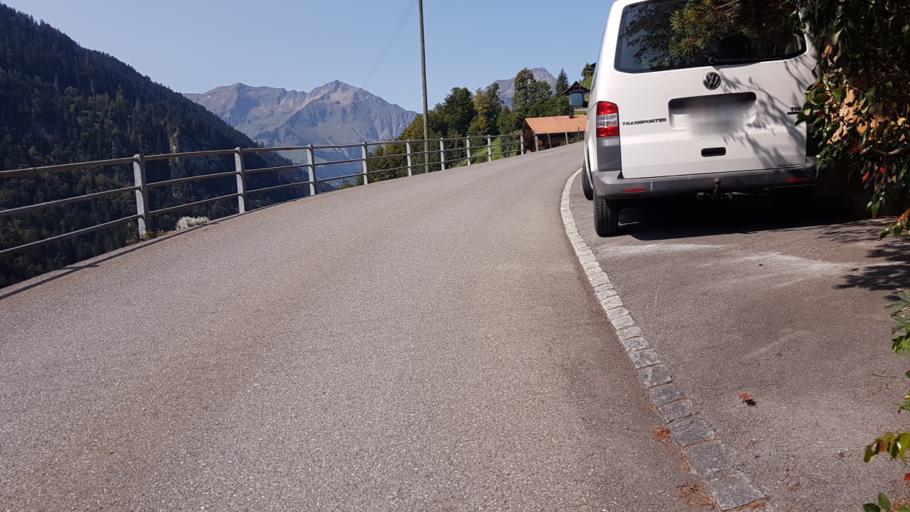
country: CH
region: Bern
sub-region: Frutigen-Niedersimmental District
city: Aeschi
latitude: 46.5917
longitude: 7.7190
